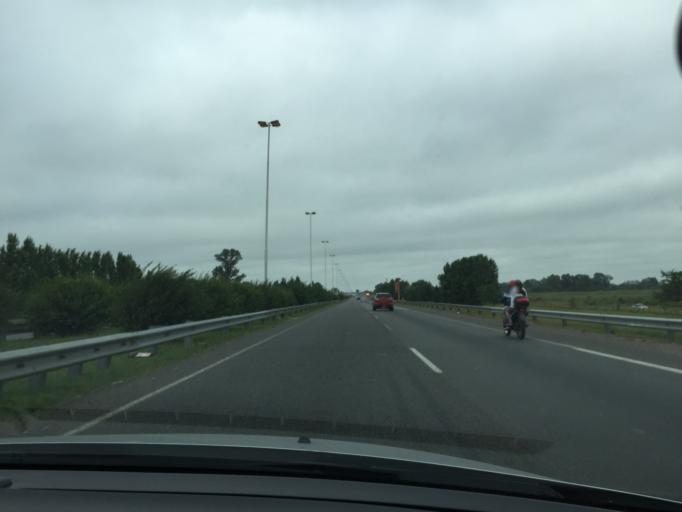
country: AR
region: Buenos Aires
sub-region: Partido de Ezeiza
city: Ezeiza
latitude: -34.8683
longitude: -58.5775
